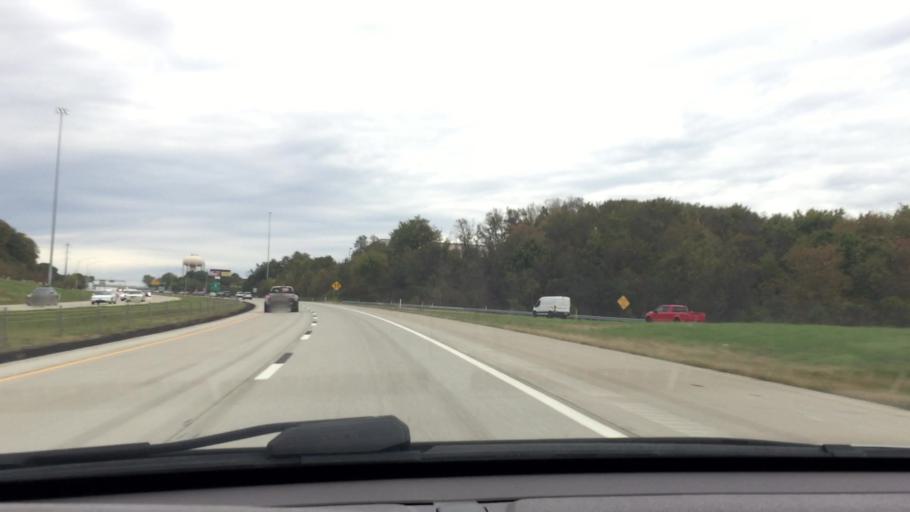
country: US
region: Pennsylvania
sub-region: Allegheny County
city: Carnot-Moon
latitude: 40.5233
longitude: -80.2727
